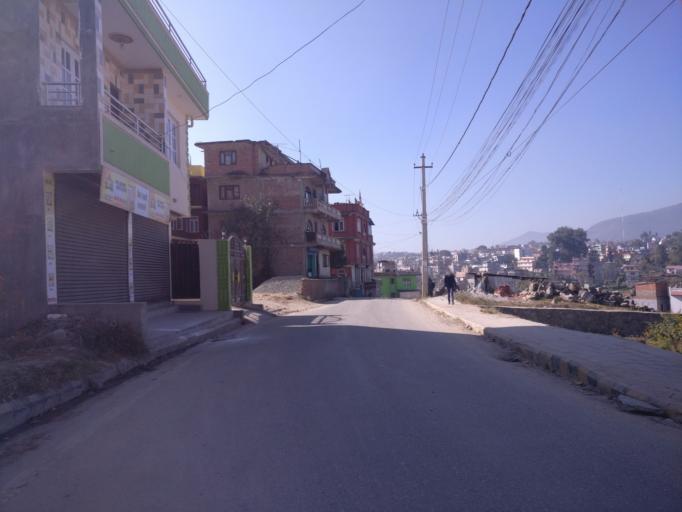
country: NP
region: Central Region
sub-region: Bagmati Zone
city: Patan
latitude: 27.6532
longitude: 85.3140
